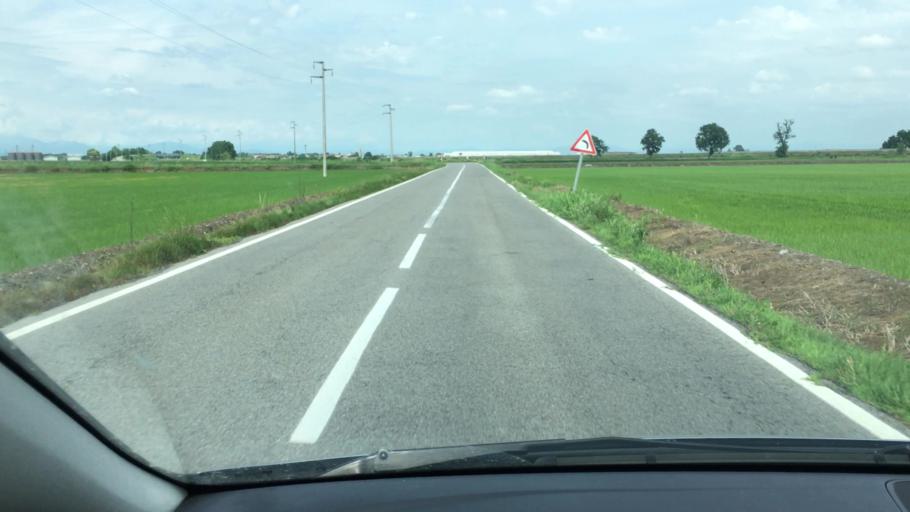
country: IT
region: Piedmont
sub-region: Provincia di Novara
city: Casalvolone
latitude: 45.4160
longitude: 8.4638
